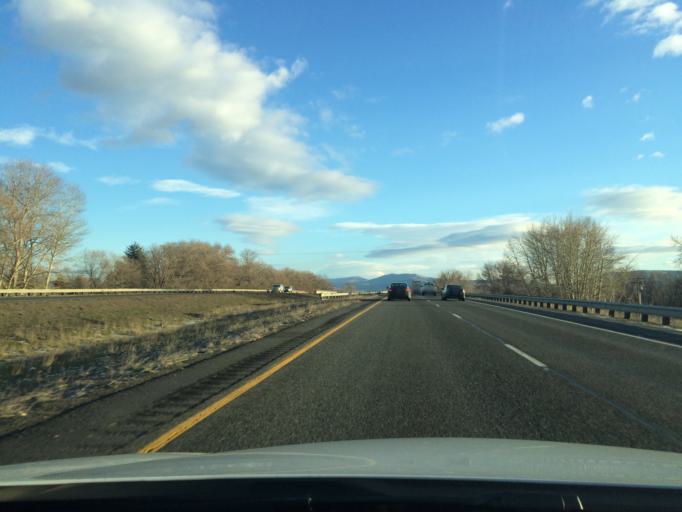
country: US
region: Washington
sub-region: Kittitas County
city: Ellensburg
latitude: 46.9821
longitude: -120.5620
